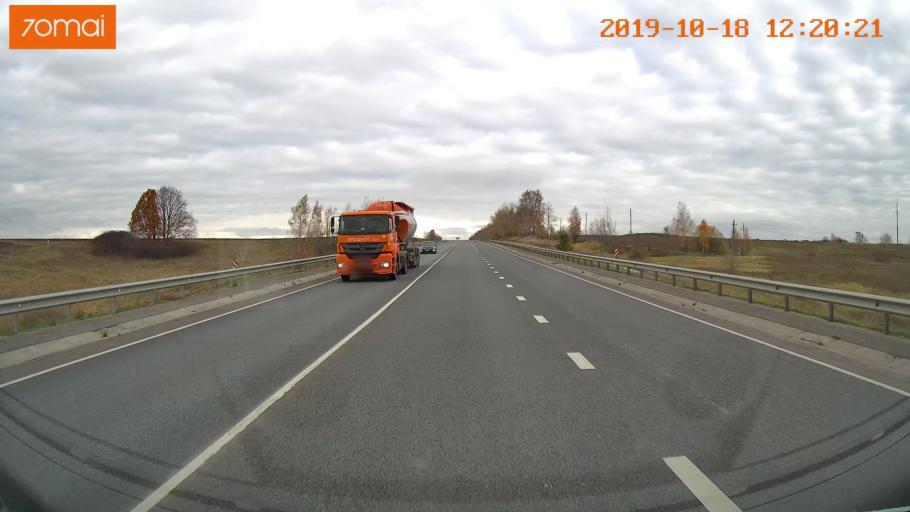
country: RU
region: Rjazan
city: Bagramovo
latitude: 54.4964
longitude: 39.4792
